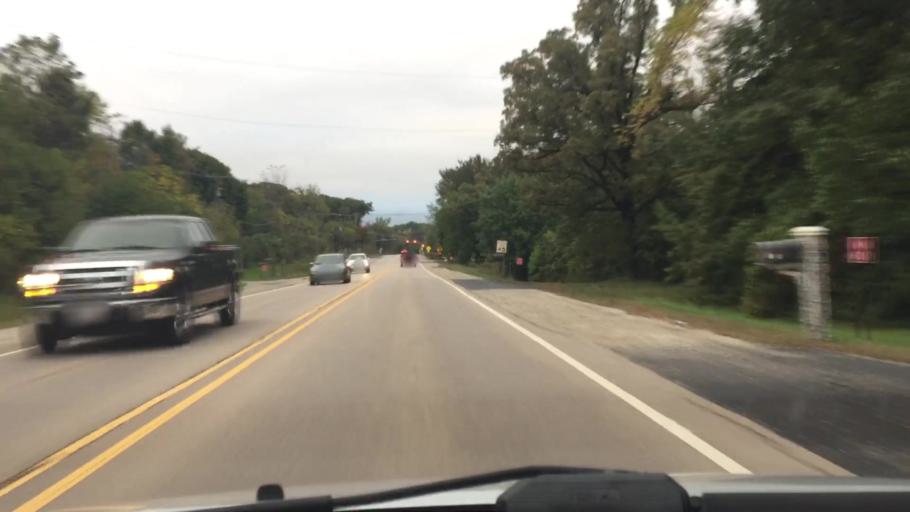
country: US
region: Illinois
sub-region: Kane County
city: Farmington
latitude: 41.9653
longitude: -88.3212
